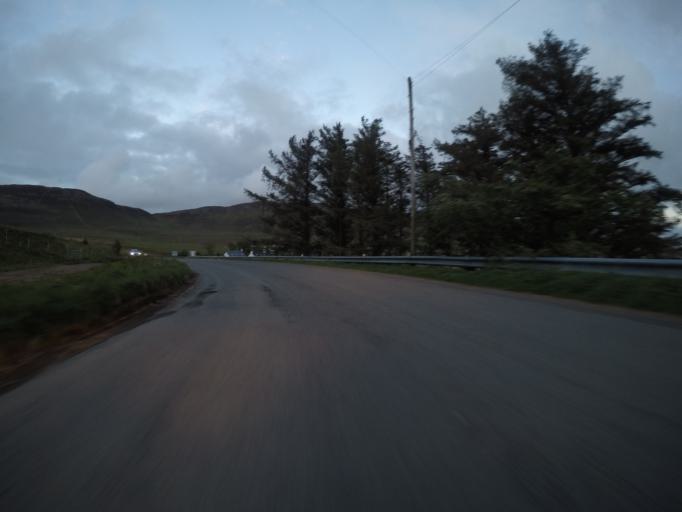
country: GB
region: Scotland
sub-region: Highland
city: Portree
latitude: 57.6218
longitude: -6.3773
